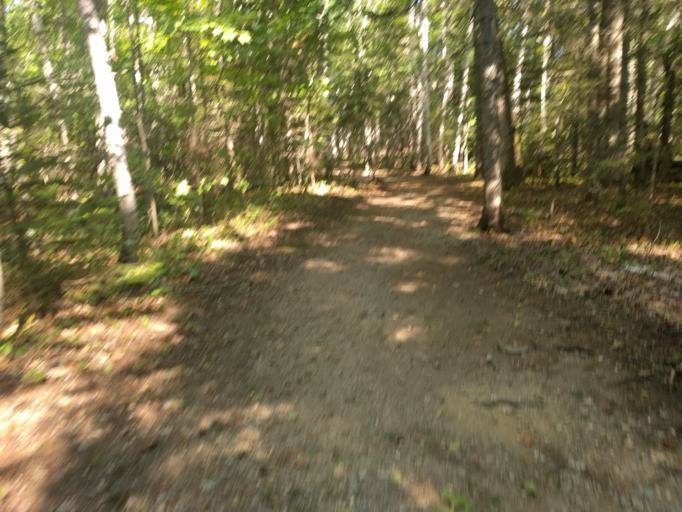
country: US
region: Maine
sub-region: Waldo County
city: Belfast
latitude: 44.4301
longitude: -68.9457
